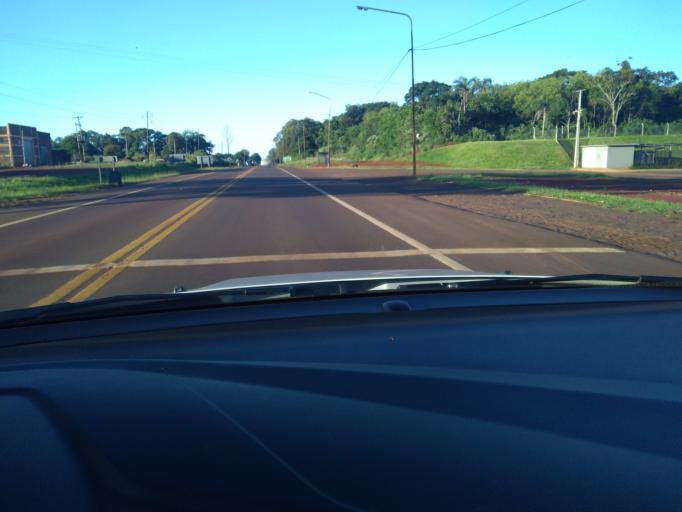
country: AR
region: Misiones
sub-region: Departamento de Obera
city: Obera
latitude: -27.4738
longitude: -55.0864
